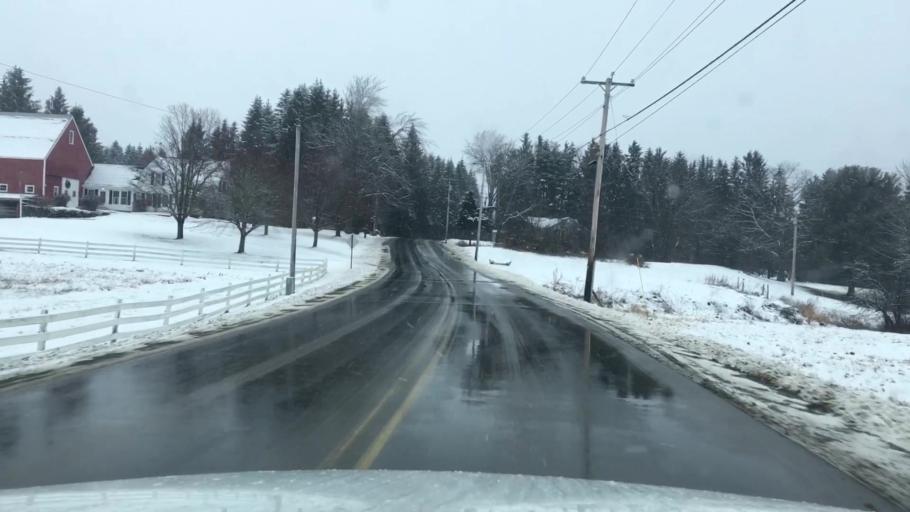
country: US
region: Maine
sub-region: Knox County
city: Warren
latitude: 44.1218
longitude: -69.2528
